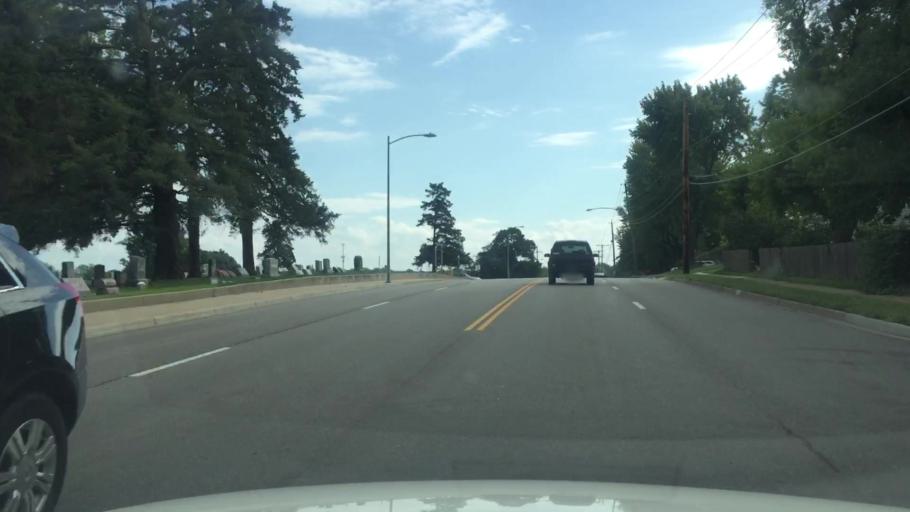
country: US
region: Kansas
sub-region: Johnson County
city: Shawnee
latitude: 39.0187
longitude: -94.7239
